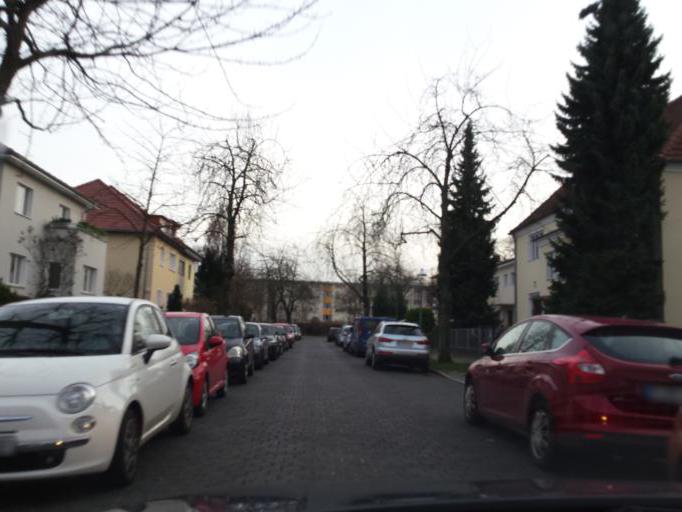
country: DE
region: Berlin
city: Zehlendorf Bezirk
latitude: 52.4358
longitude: 13.2691
